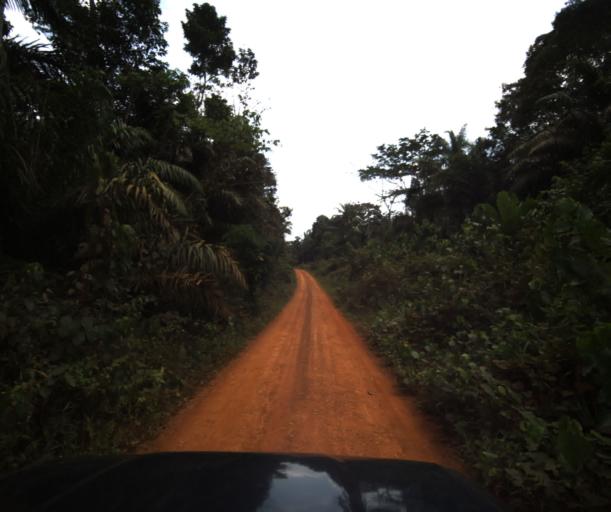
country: CM
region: Centre
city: Eseka
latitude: 3.5447
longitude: 10.9280
